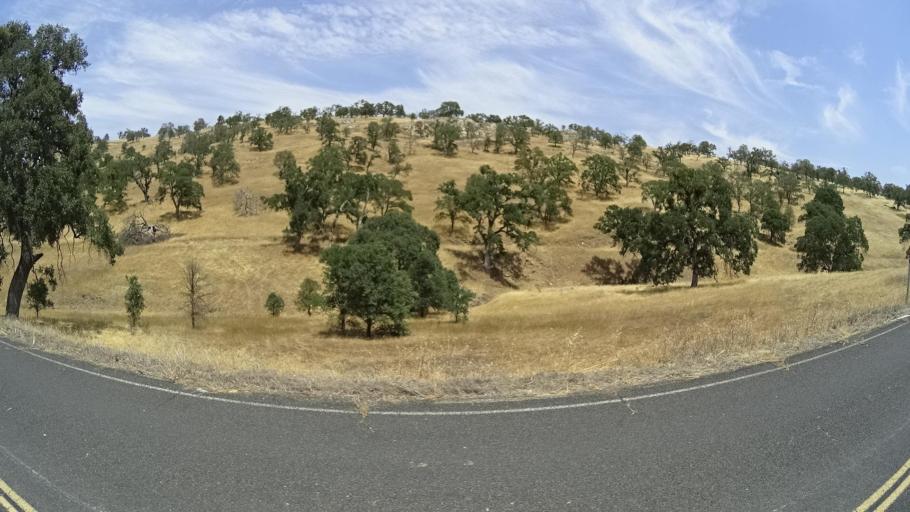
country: US
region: California
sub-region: Tuolumne County
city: Jamestown
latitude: 37.6649
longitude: -120.3517
